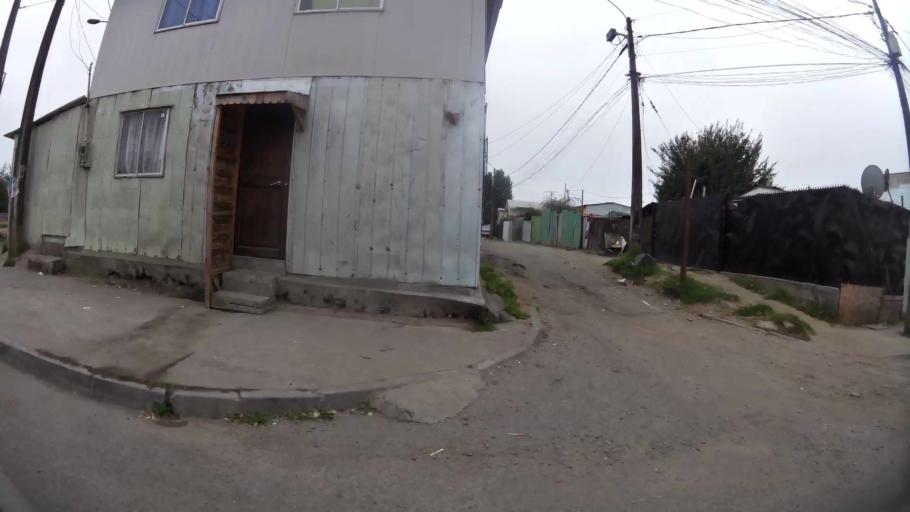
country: CL
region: Biobio
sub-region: Provincia de Concepcion
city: Concepcion
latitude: -36.8401
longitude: -73.0593
